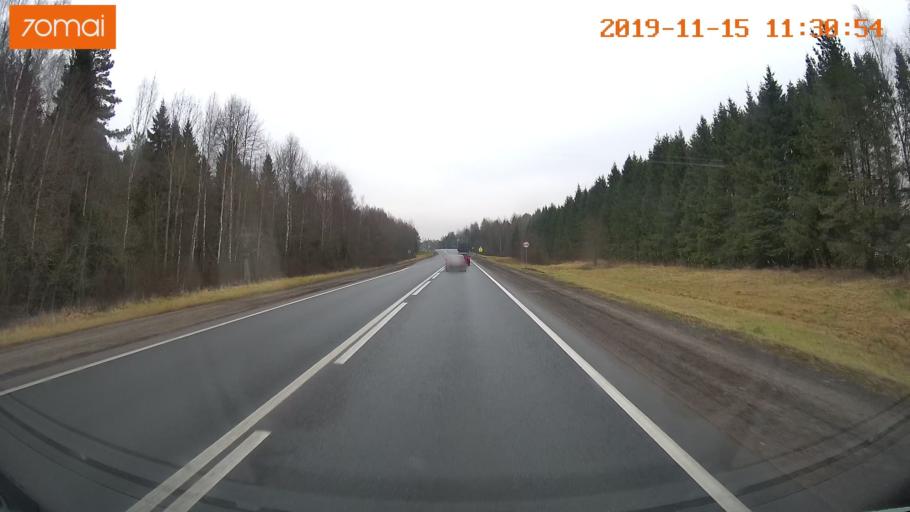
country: RU
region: Vologda
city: Molochnoye
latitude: 59.1791
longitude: 39.5393
